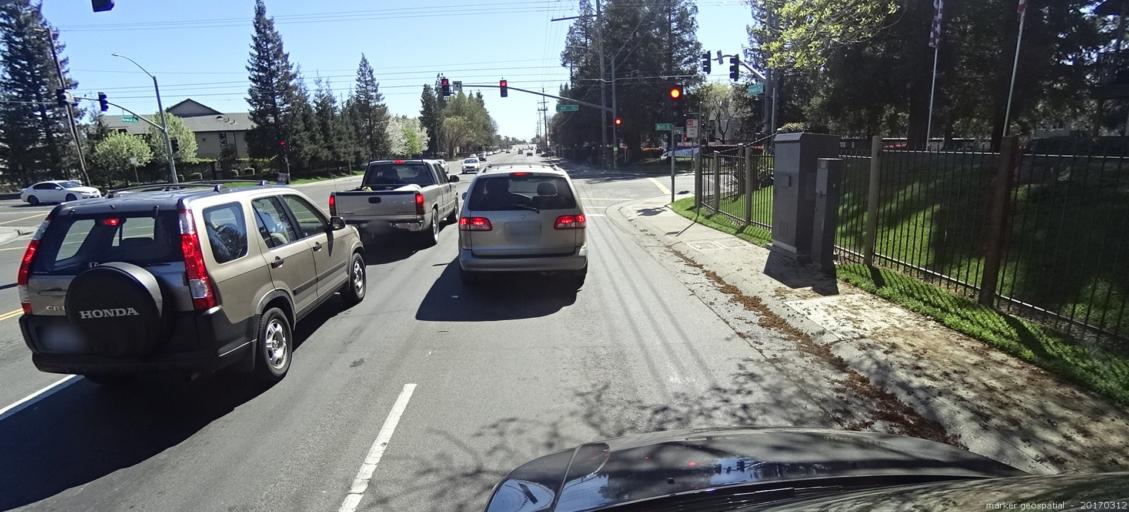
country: US
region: California
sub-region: Sacramento County
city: Rio Linda
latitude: 38.6479
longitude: -121.4570
